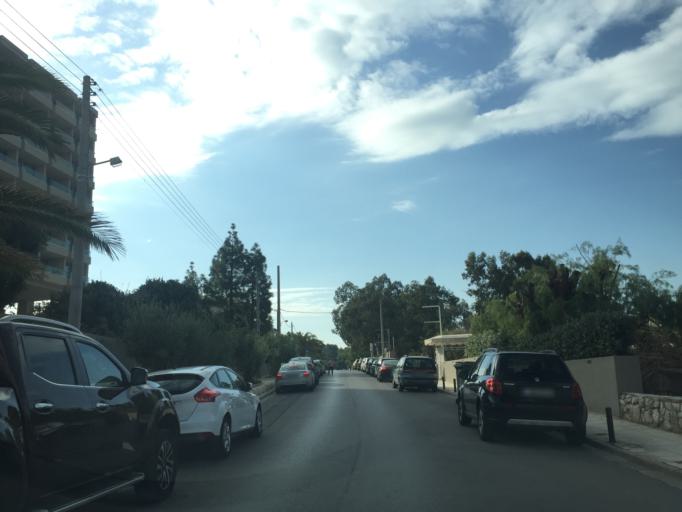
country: GR
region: Attica
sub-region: Nomarchia Anatolikis Attikis
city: Voula
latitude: 37.8288
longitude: 23.7707
